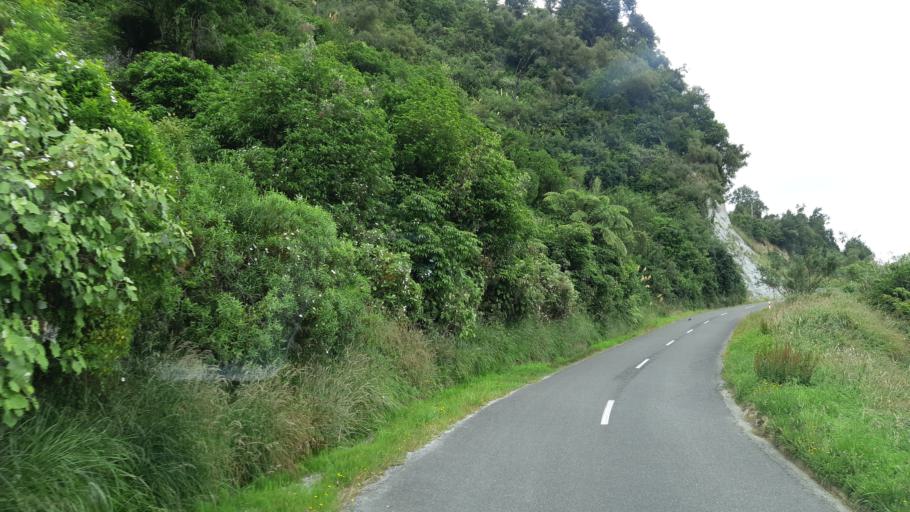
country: NZ
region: Manawatu-Wanganui
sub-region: Palmerston North City
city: Palmerston North
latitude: -39.9403
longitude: 175.9172
